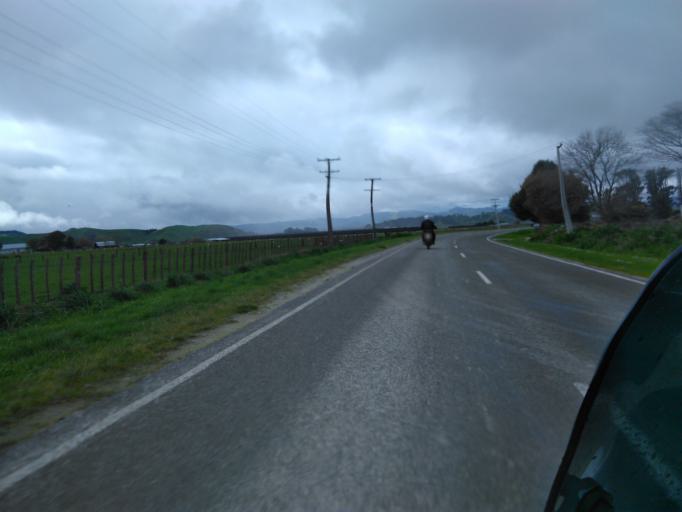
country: NZ
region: Gisborne
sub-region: Gisborne District
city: Gisborne
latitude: -38.6463
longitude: 177.8523
